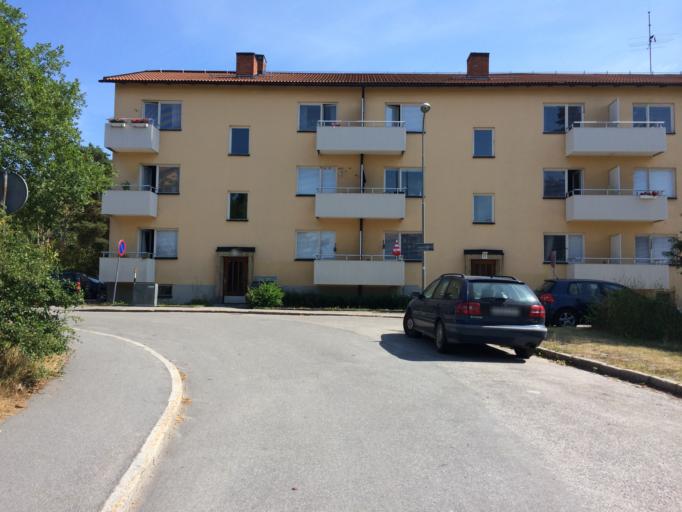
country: SE
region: Stockholm
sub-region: Huddinge Kommun
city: Segeltorp
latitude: 59.2944
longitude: 17.9831
